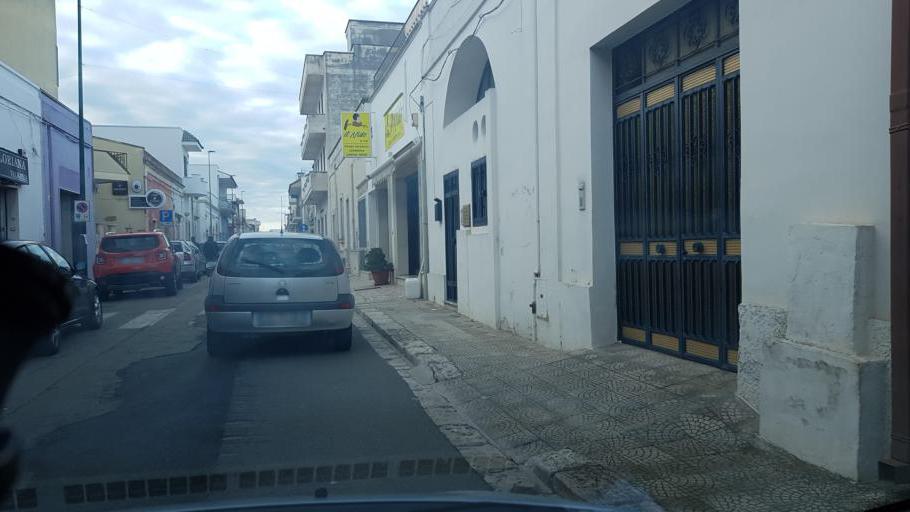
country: IT
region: Apulia
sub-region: Provincia di Lecce
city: Veglie
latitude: 40.3335
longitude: 17.9666
